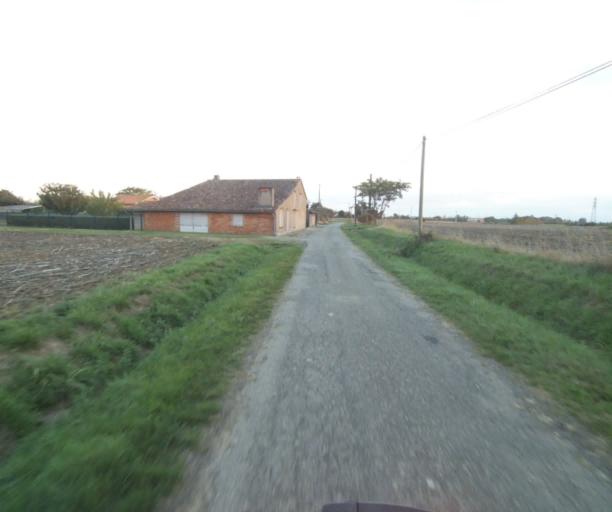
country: FR
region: Midi-Pyrenees
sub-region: Departement du Tarn-et-Garonne
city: Verdun-sur-Garonne
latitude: 43.8403
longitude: 1.2425
